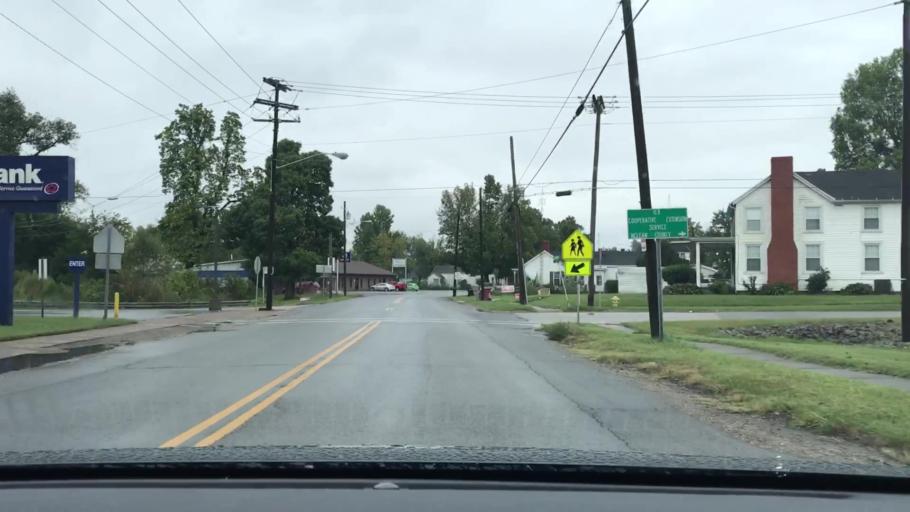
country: US
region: Kentucky
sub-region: McLean County
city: Calhoun
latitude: 37.5428
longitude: -87.2592
